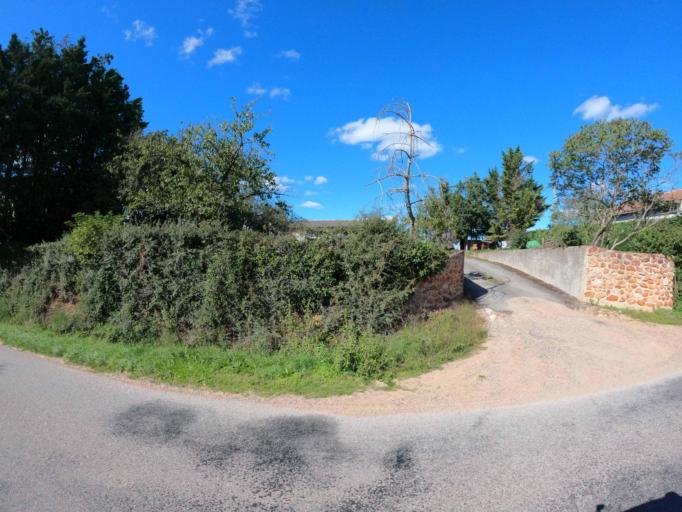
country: FR
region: Auvergne
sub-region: Departement de l'Allier
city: Buxieres-les-Mines
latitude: 46.3977
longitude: 2.8864
